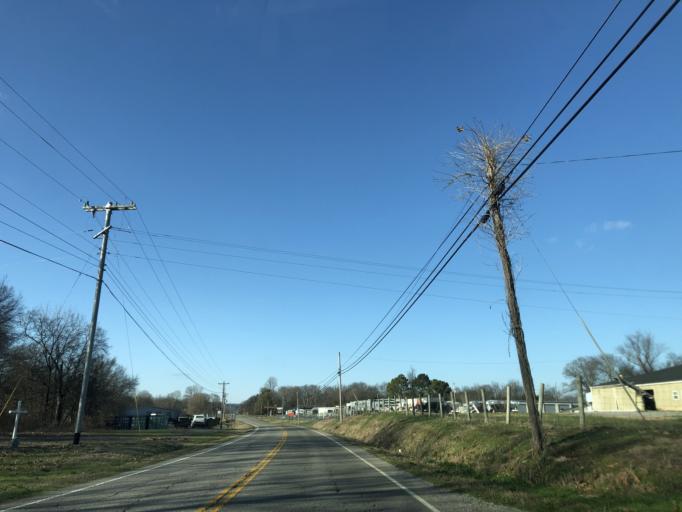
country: US
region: Tennessee
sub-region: Sumner County
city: Gallatin
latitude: 36.4145
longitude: -86.4537
